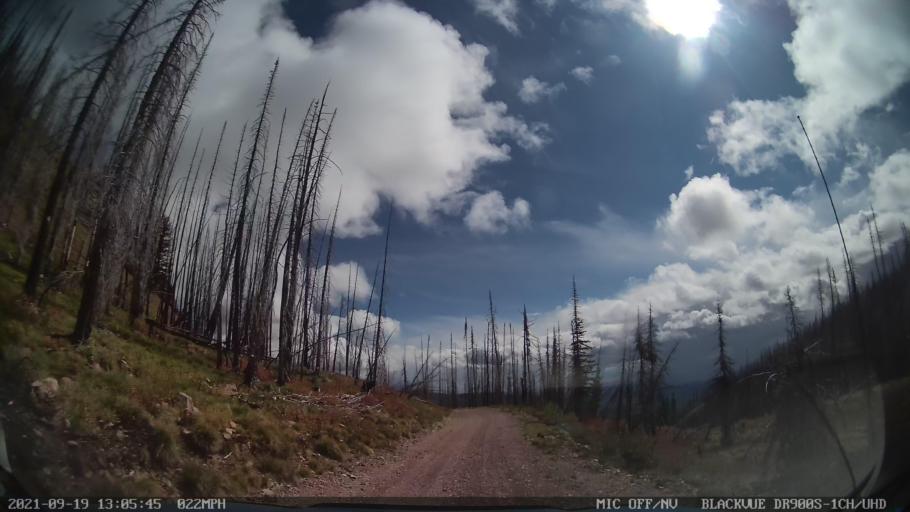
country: US
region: Montana
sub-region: Missoula County
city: Seeley Lake
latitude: 47.1906
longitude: -113.3504
